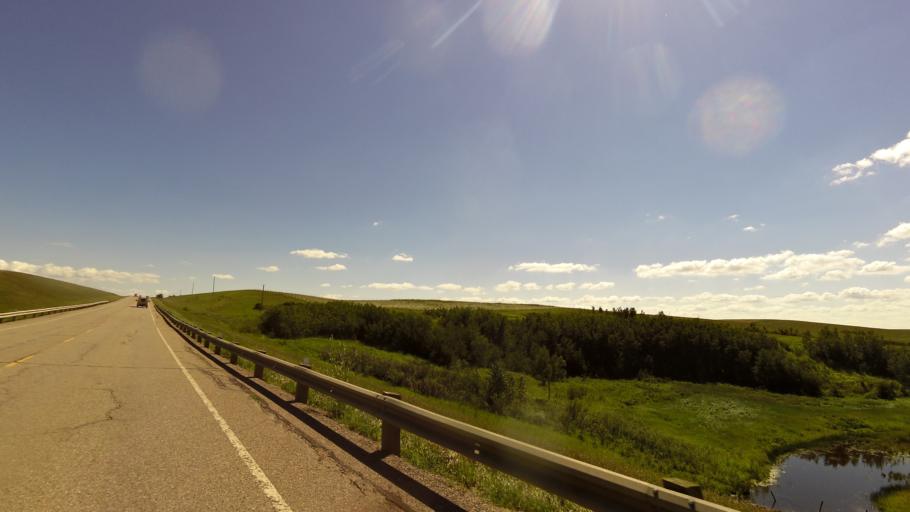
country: CA
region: Saskatchewan
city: Lloydminster
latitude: 52.8417
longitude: -110.0313
